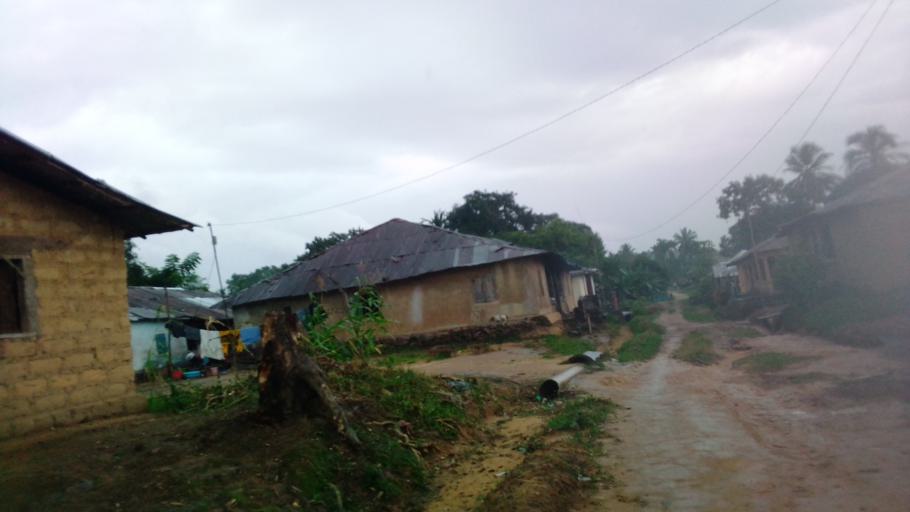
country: SL
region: Northern Province
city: Lunsar
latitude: 8.6811
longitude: -12.5291
